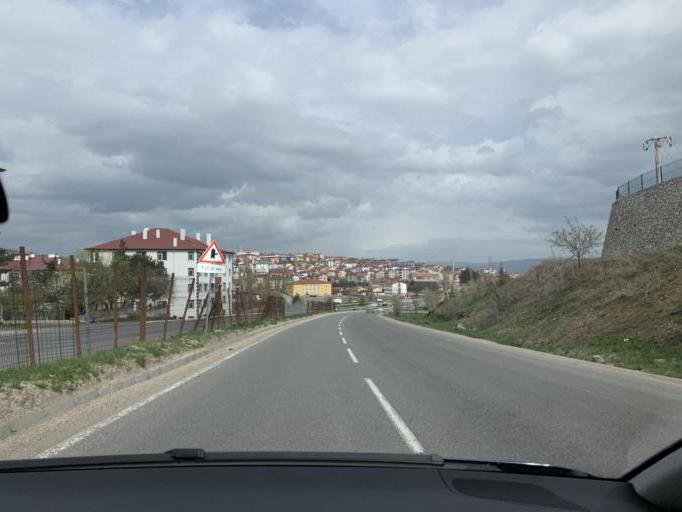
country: TR
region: Bolu
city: Gerede
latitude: 40.7965
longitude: 32.1989
